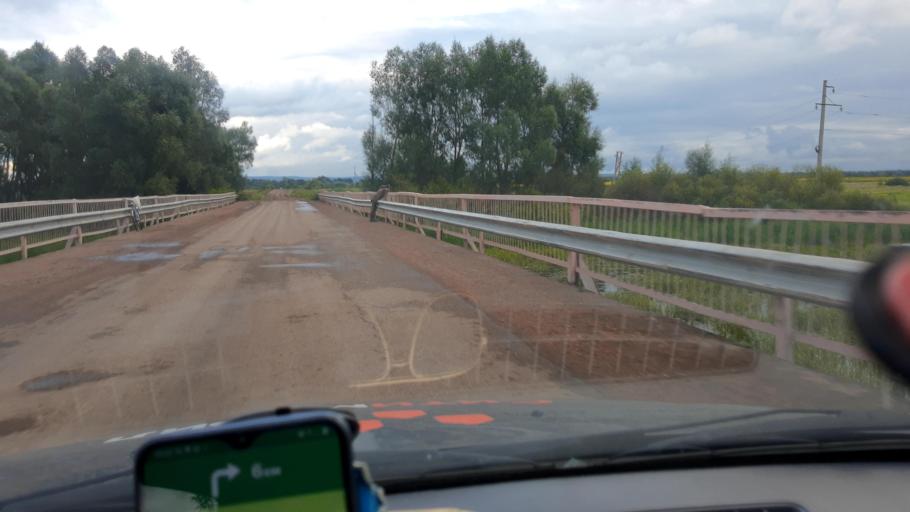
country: RU
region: Bashkortostan
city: Karmaskaly
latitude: 53.9895
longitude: 56.2908
